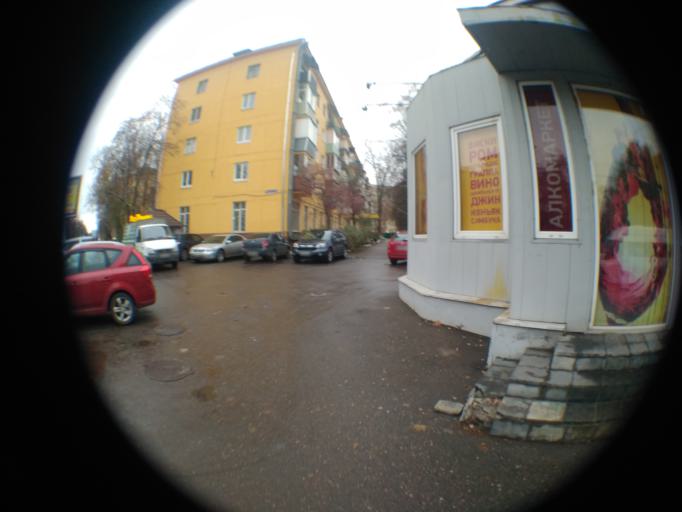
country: RU
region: Moskovskaya
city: Zhukovskiy
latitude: 55.5913
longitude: 38.1302
